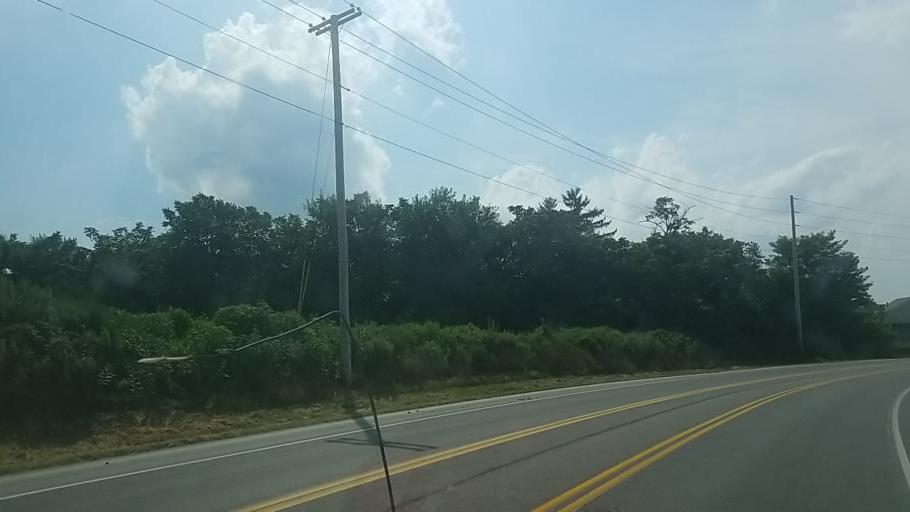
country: US
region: Pennsylvania
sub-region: Lancaster County
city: Strasburg
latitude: 39.9833
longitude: -76.1710
